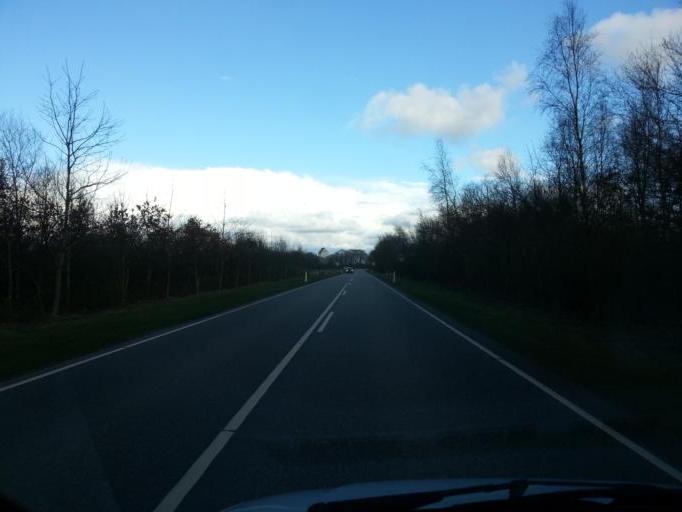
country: DK
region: Central Jutland
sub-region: Ringkobing-Skjern Kommune
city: Tarm
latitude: 55.8866
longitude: 8.5178
